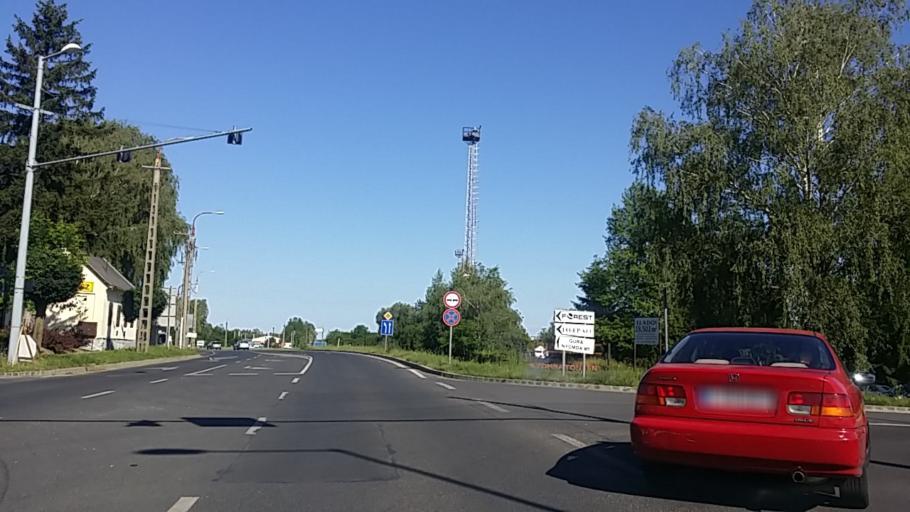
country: HU
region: Zala
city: Zalaegerszeg
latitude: 46.8530
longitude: 16.8125
